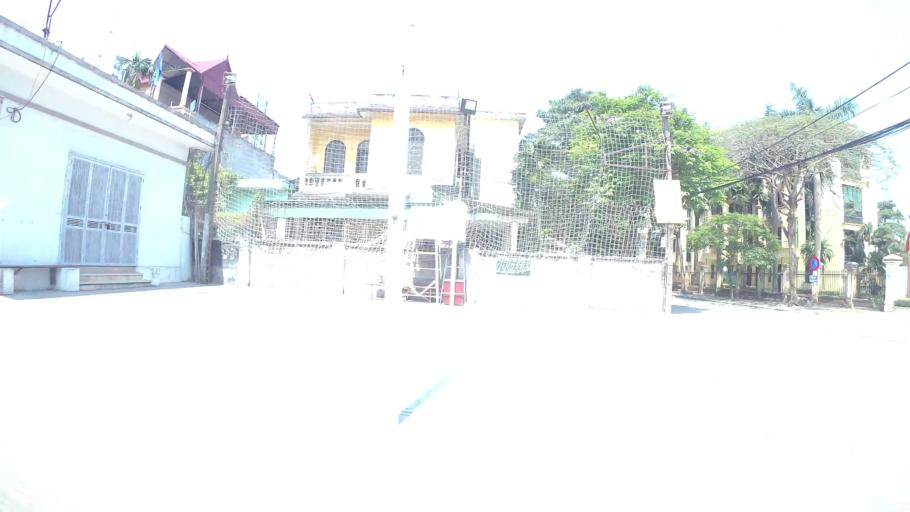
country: VN
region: Ha Noi
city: Hoan Kiem
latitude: 21.0548
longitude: 105.8771
